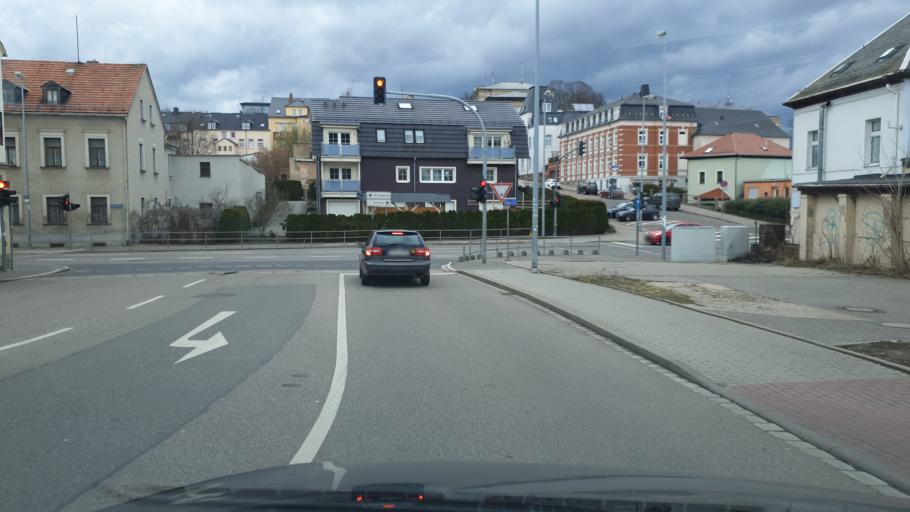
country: DE
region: Saxony
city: Mittweida
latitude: 50.9857
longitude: 12.9725
